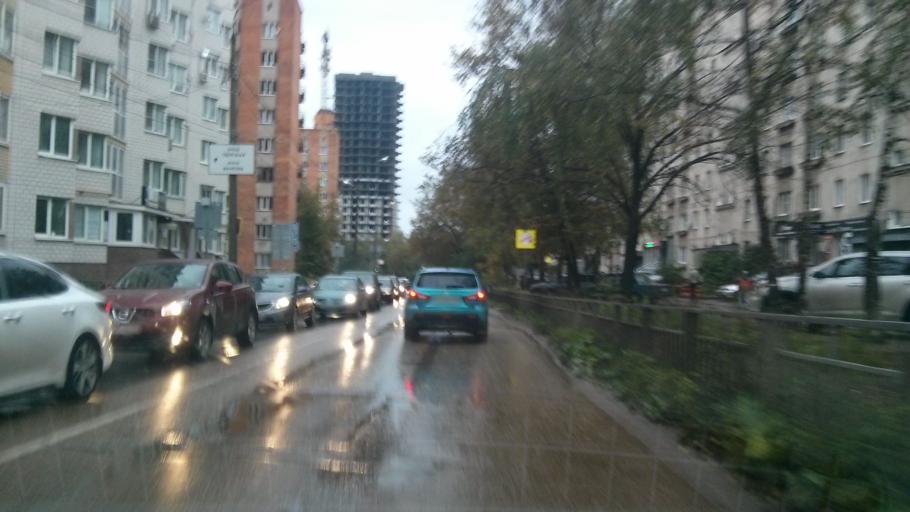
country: RU
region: Nizjnij Novgorod
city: Nizhniy Novgorod
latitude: 56.3061
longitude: 43.9944
